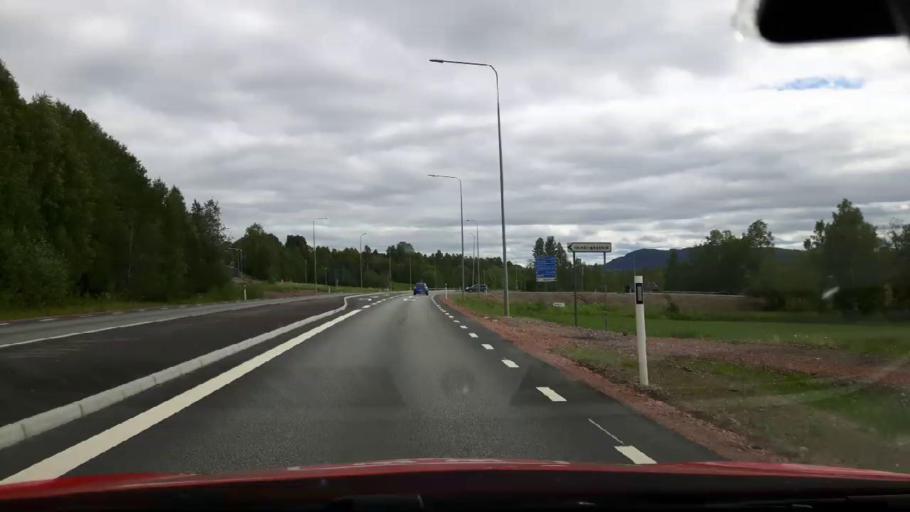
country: SE
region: Jaemtland
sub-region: Ragunda Kommun
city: Hammarstrand
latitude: 63.1190
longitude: 16.3640
